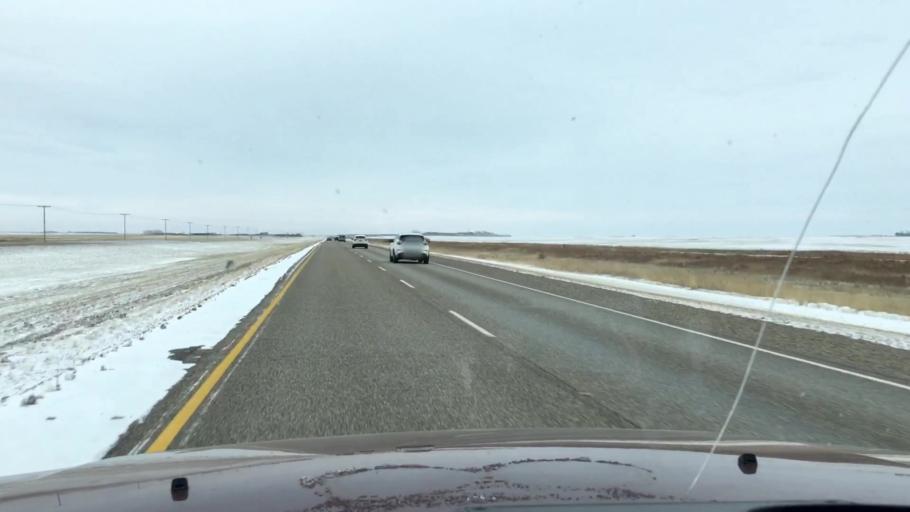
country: CA
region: Saskatchewan
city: Moose Jaw
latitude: 50.9966
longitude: -105.7598
